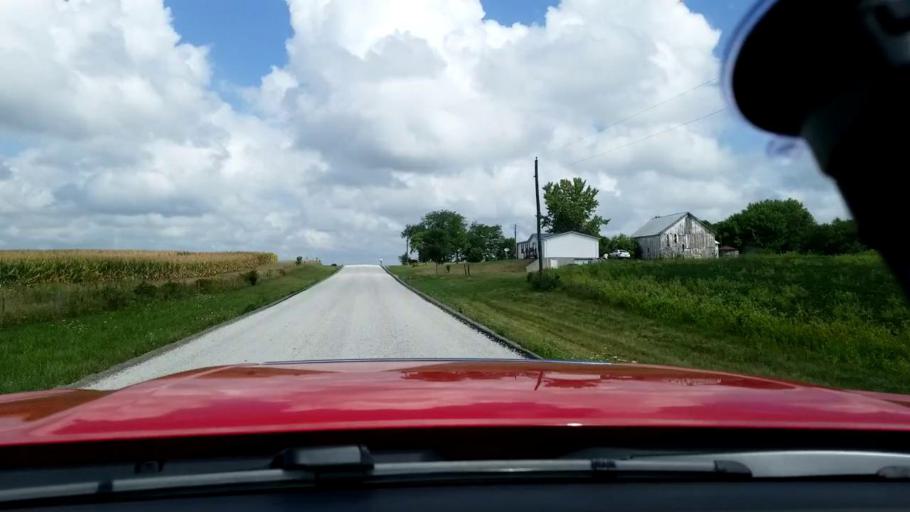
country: US
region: Iowa
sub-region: Decatur County
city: Lamoni
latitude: 40.6368
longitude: -94.0531
